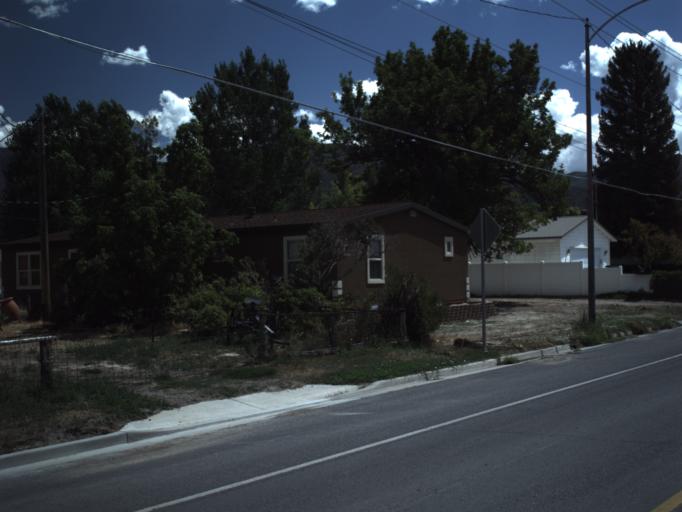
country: US
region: Utah
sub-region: Sanpete County
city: Ephraim
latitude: 39.3612
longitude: -111.5772
